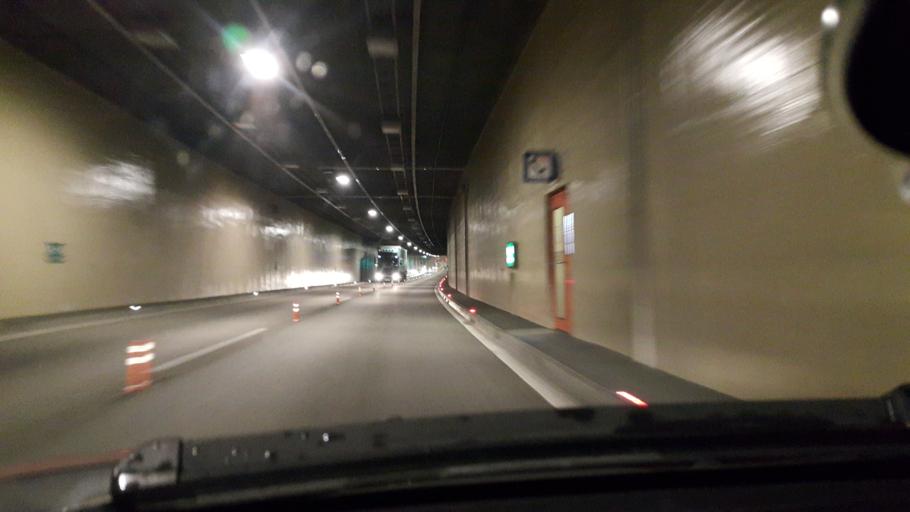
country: AT
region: Carinthia
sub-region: Klagenfurt am Woerthersee
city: Klagenfurt am Woerthersee
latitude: 46.6486
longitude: 14.3283
